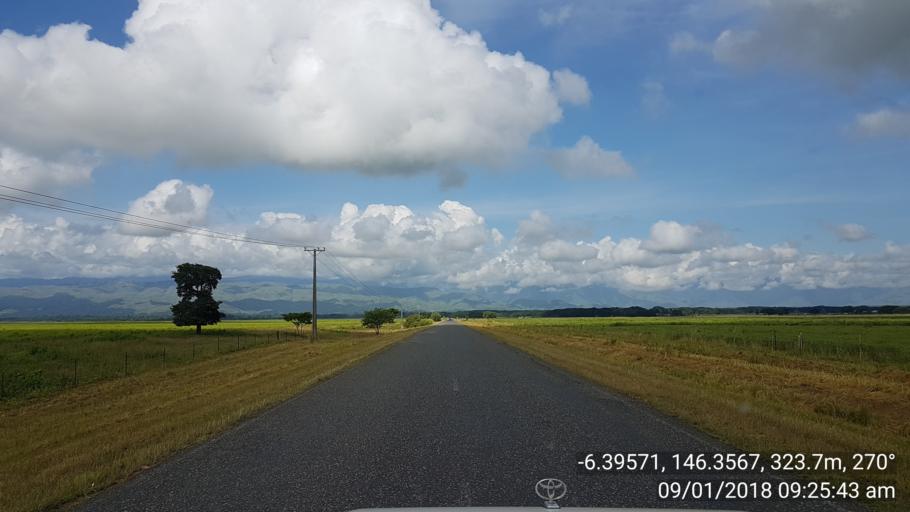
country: PG
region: Eastern Highlands
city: Kainantu
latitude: -6.3958
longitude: 146.3569
